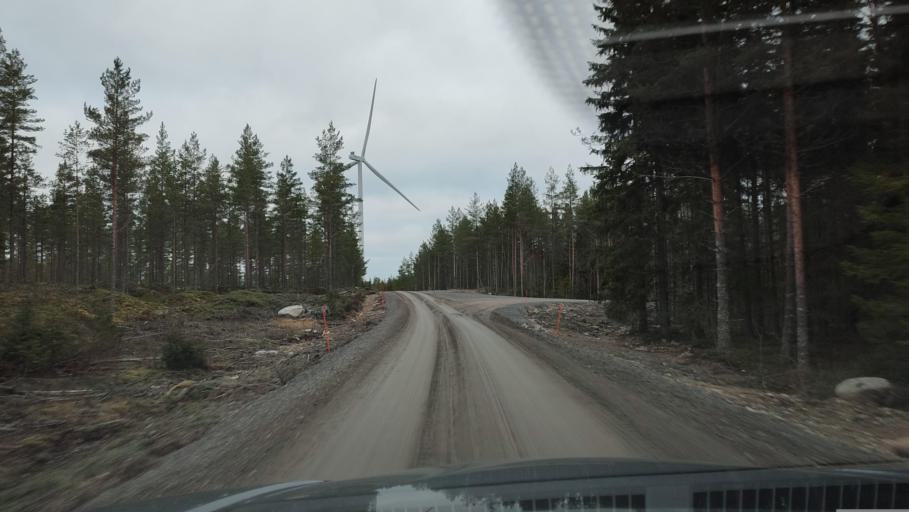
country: FI
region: Southern Ostrobothnia
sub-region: Suupohja
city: Karijoki
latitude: 62.1987
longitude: 21.5901
